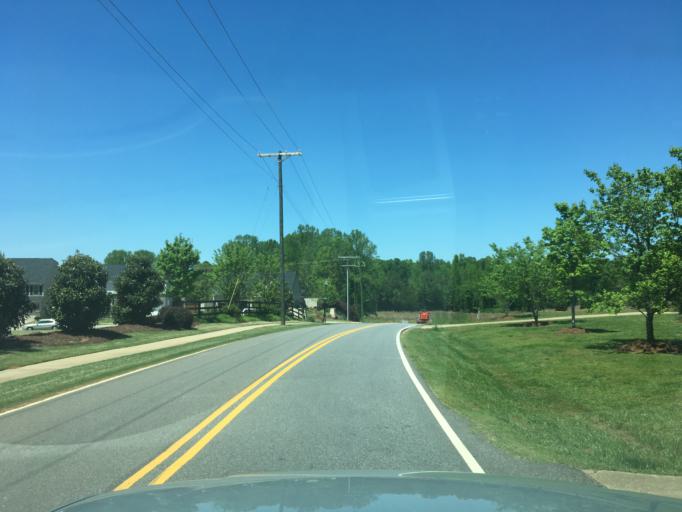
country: US
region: South Carolina
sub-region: Spartanburg County
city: Duncan
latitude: 34.8614
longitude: -82.1498
